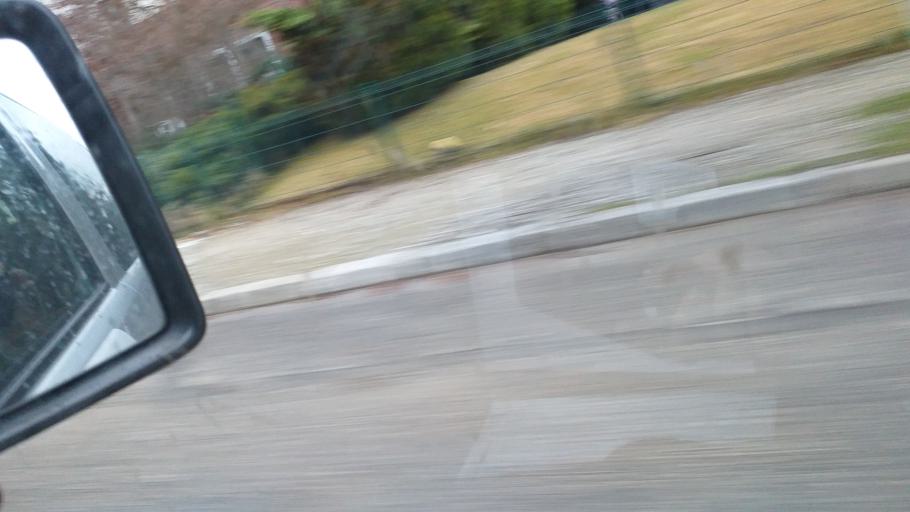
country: TR
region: Ankara
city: Batikent
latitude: 39.8778
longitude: 32.7153
